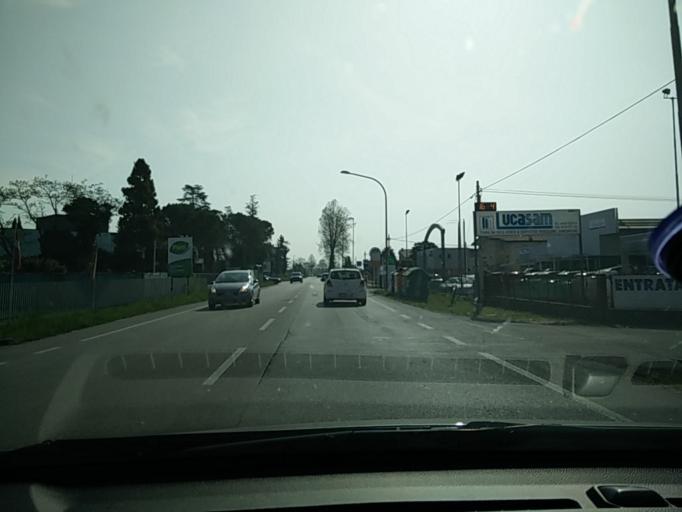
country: IT
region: Friuli Venezia Giulia
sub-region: Provincia di Pordenone
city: Pordenone
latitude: 45.9478
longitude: 12.6837
